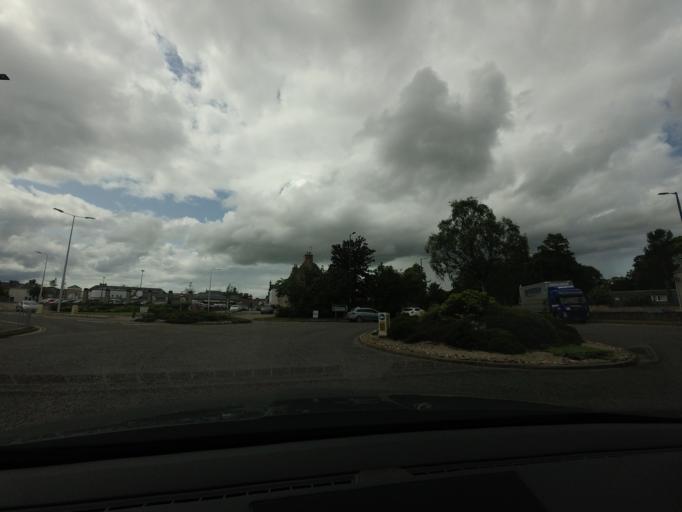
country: GB
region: Scotland
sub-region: Moray
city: Elgin
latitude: 57.6487
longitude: -3.3079
